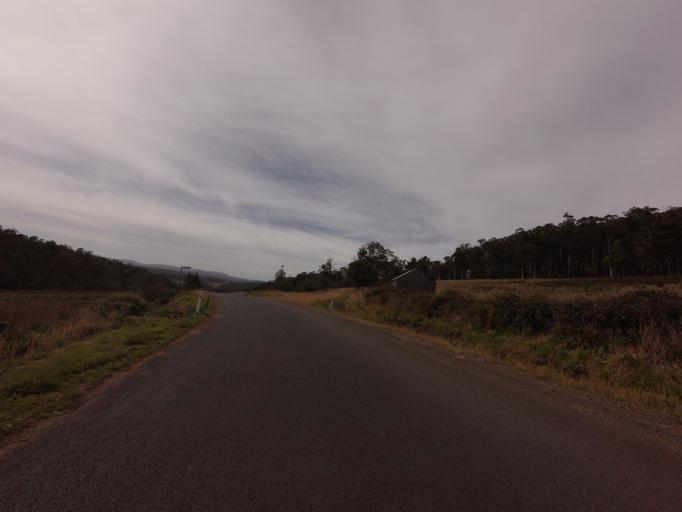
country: AU
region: Tasmania
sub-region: Sorell
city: Sorell
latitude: -42.4468
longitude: 147.5573
